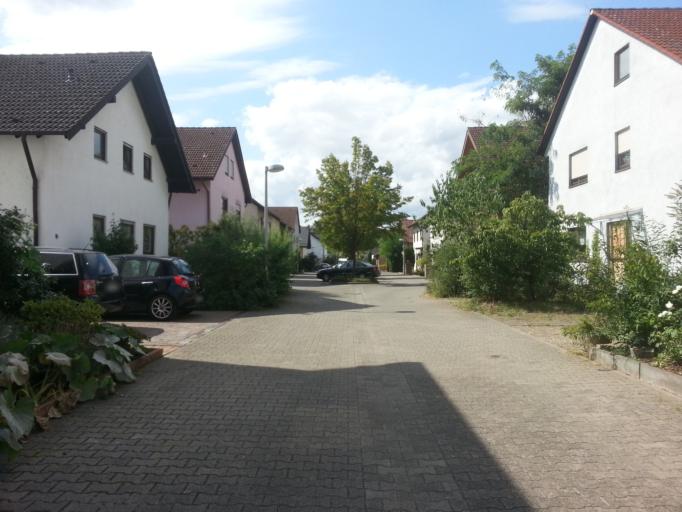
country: DE
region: Baden-Wuerttemberg
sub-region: Karlsruhe Region
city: Mannheim
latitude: 49.5057
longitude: 8.4963
